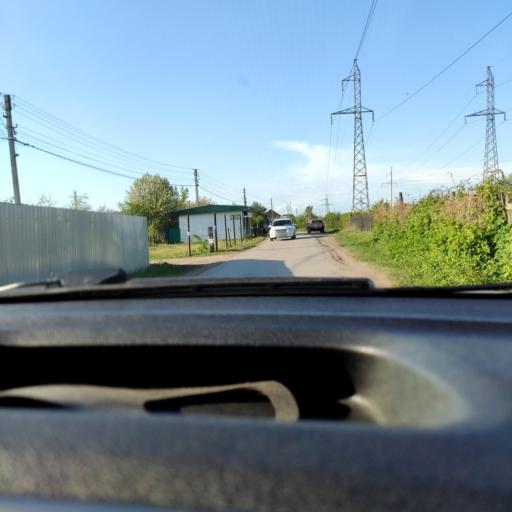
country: RU
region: Samara
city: Tol'yatti
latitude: 53.5829
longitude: 49.3001
